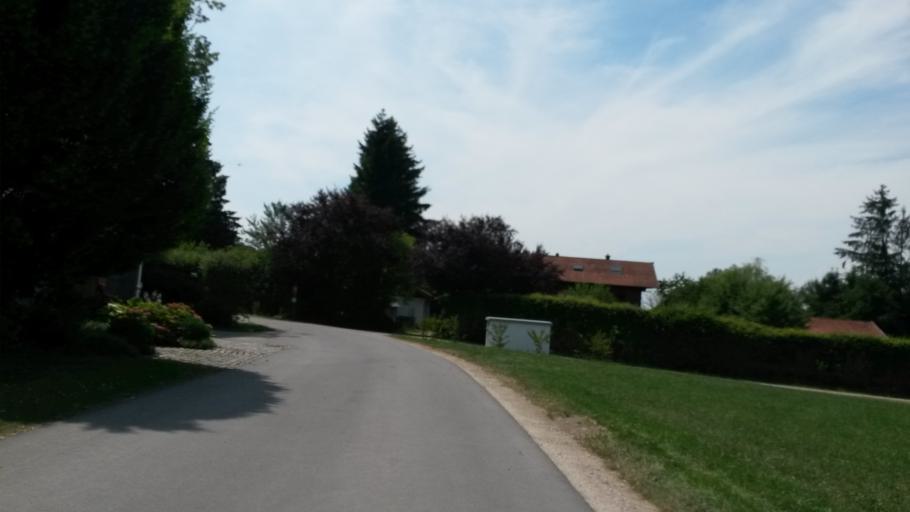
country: DE
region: Bavaria
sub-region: Upper Bavaria
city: Seeon-Seebruck
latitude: 47.9421
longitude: 12.4931
